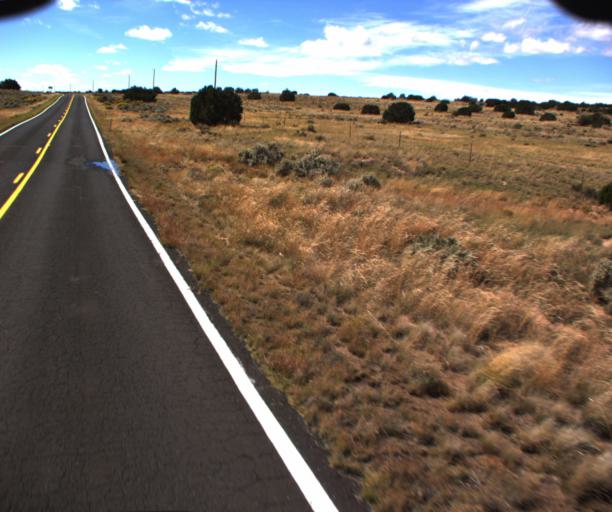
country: US
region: Arizona
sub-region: Apache County
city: Houck
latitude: 34.9496
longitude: -109.1693
